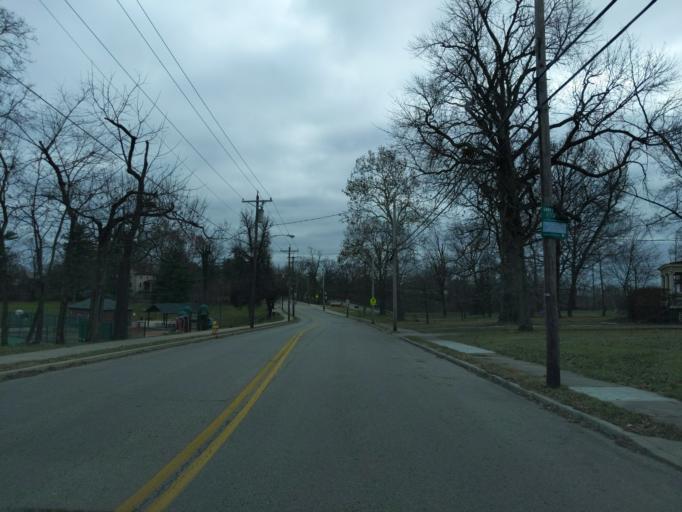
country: US
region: Ohio
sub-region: Hamilton County
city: North College Hill
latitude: 39.1940
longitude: -84.5508
